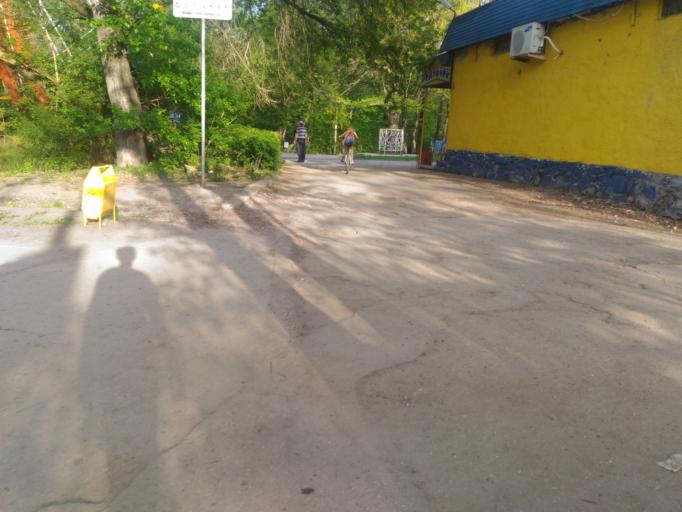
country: RU
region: Ulyanovsk
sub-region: Ulyanovskiy Rayon
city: Ulyanovsk
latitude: 54.2759
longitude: 48.3407
